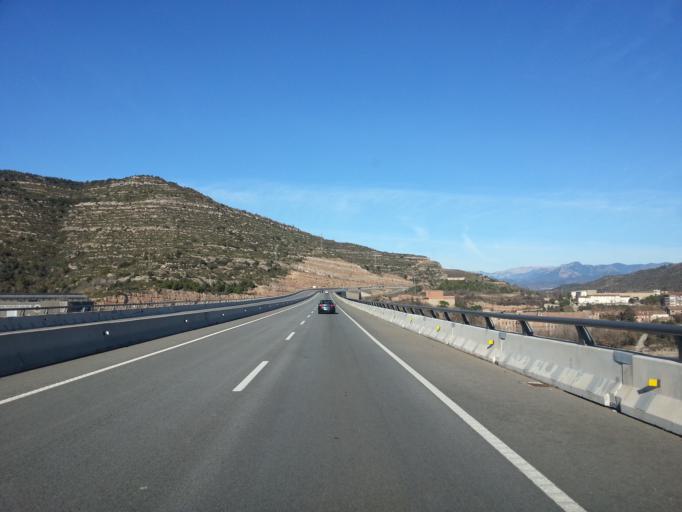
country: ES
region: Catalonia
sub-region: Provincia de Barcelona
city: Puig-reig
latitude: 41.9820
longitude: 1.8858
